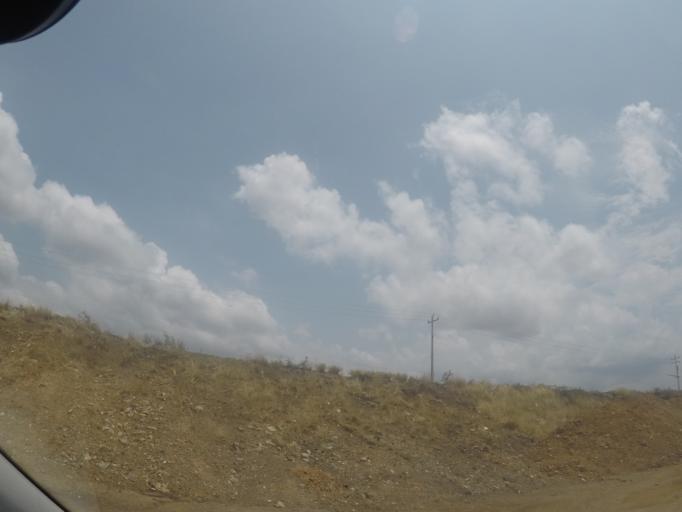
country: MX
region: Oaxaca
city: El Espinal
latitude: 16.5563
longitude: -94.9486
